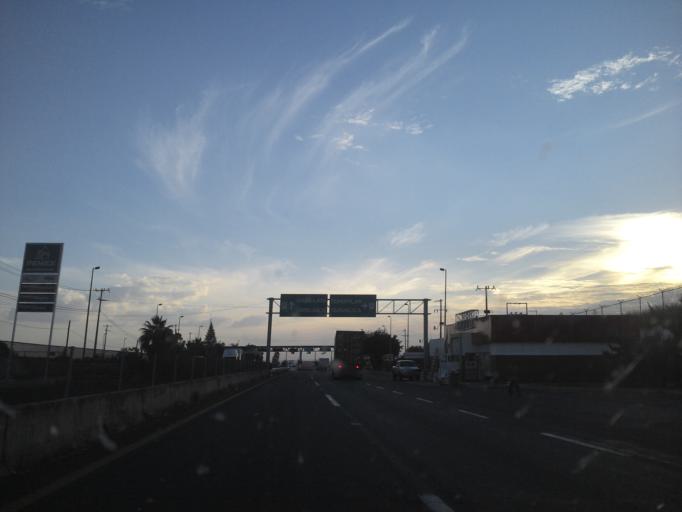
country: MX
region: Jalisco
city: Tepatitlan de Morelos
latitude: 20.8264
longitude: -102.7940
